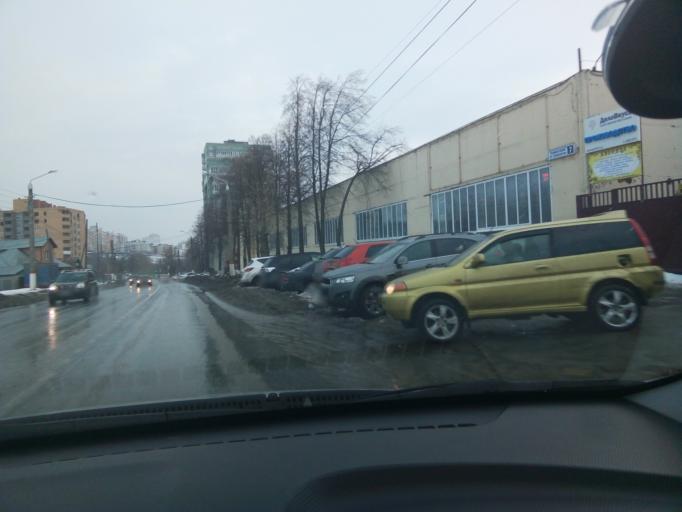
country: RU
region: Chuvashia
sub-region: Cheboksarskiy Rayon
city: Cheboksary
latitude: 56.1328
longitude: 47.2219
